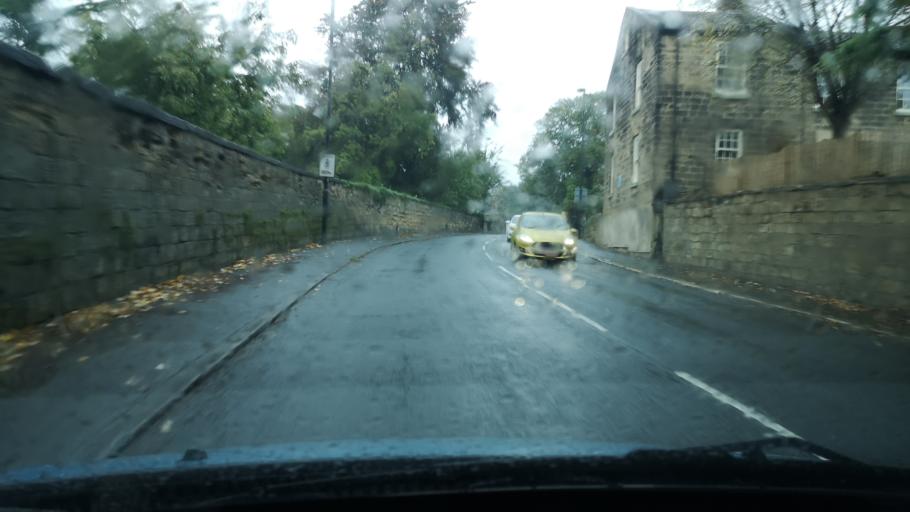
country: GB
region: England
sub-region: City and Borough of Wakefield
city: Low Ackworth
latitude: 53.6481
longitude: -1.3327
